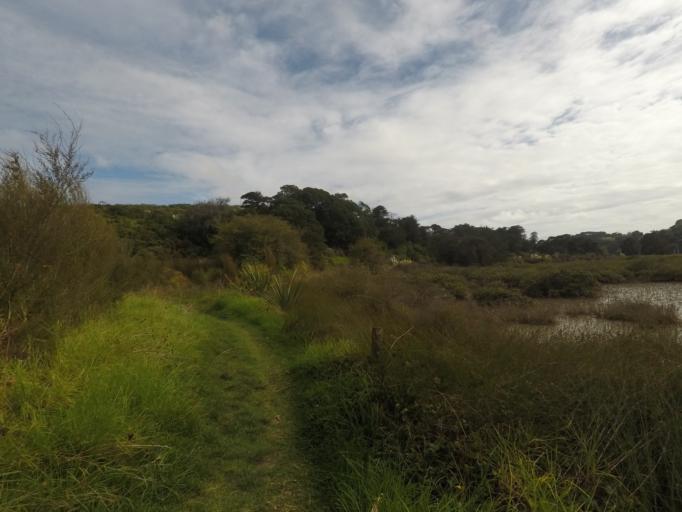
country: NZ
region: Auckland
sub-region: Auckland
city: Rothesay Bay
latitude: -36.6436
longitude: 174.7228
